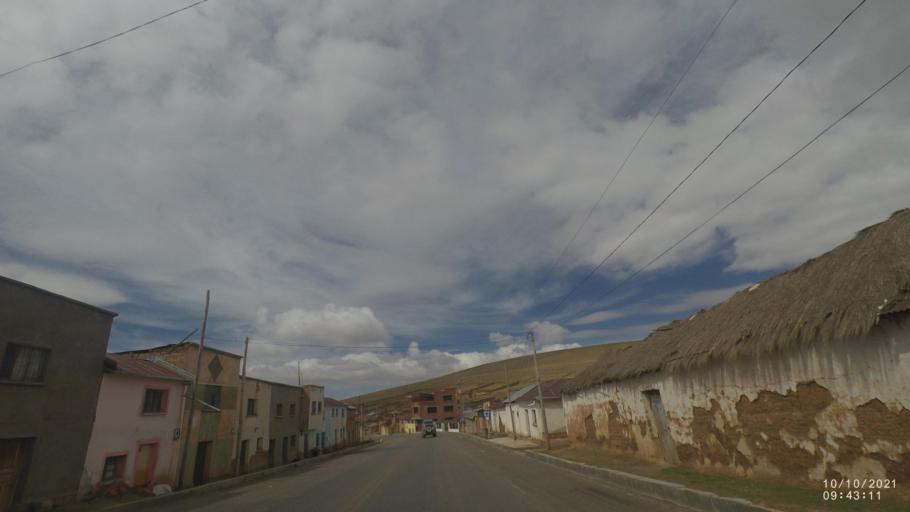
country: BO
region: La Paz
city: Quime
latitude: -17.1480
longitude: -67.3452
